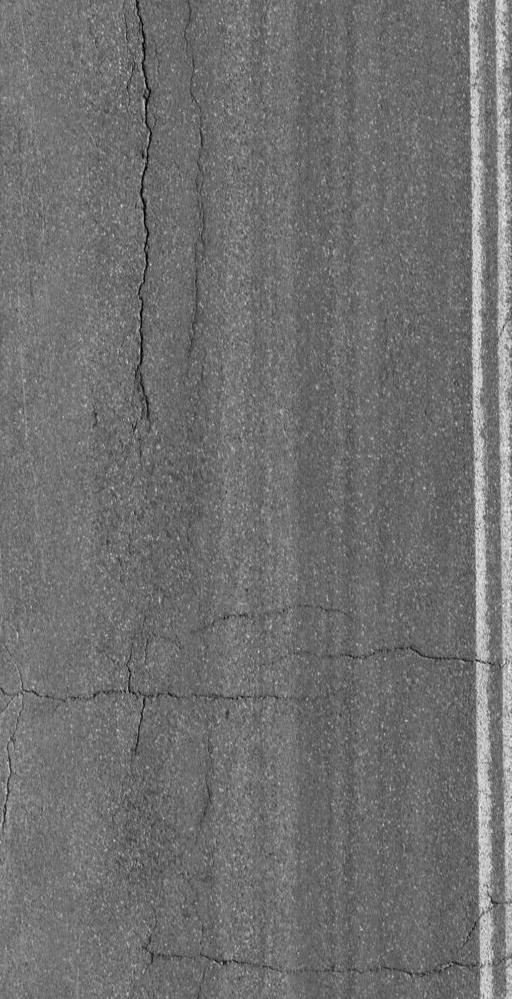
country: US
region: Vermont
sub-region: Orange County
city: Randolph
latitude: 43.8516
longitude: -72.7394
